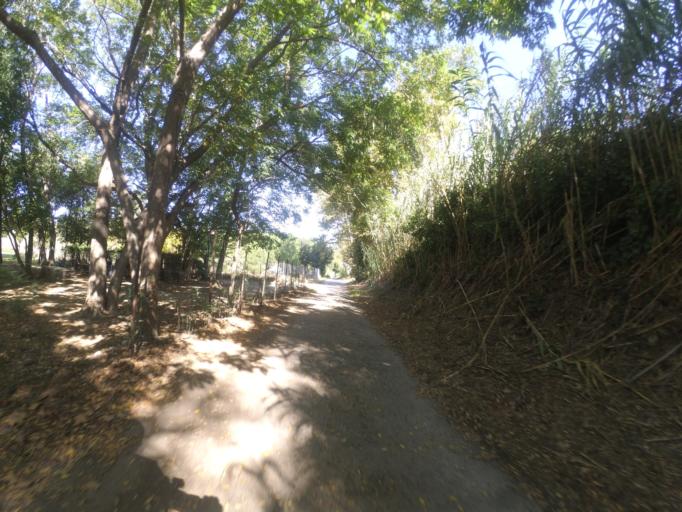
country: FR
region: Languedoc-Roussillon
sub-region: Departement des Pyrenees-Orientales
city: Pezilla-la-Riviere
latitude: 42.6864
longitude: 2.7680
